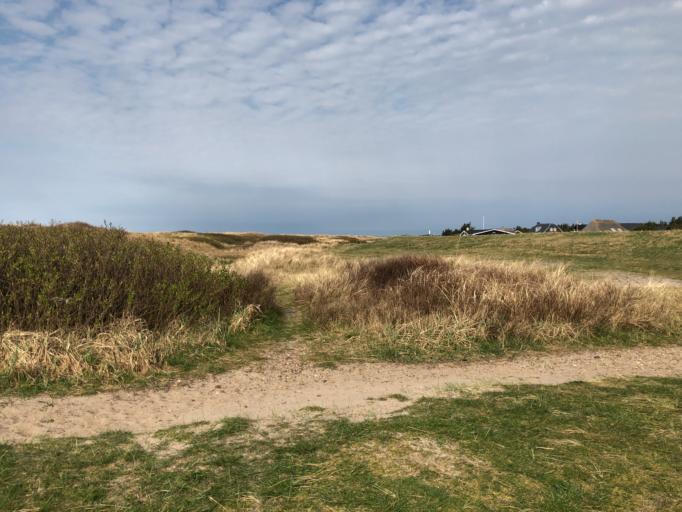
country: DK
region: South Denmark
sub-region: Varde Kommune
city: Oksbol
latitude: 55.5446
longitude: 8.1302
